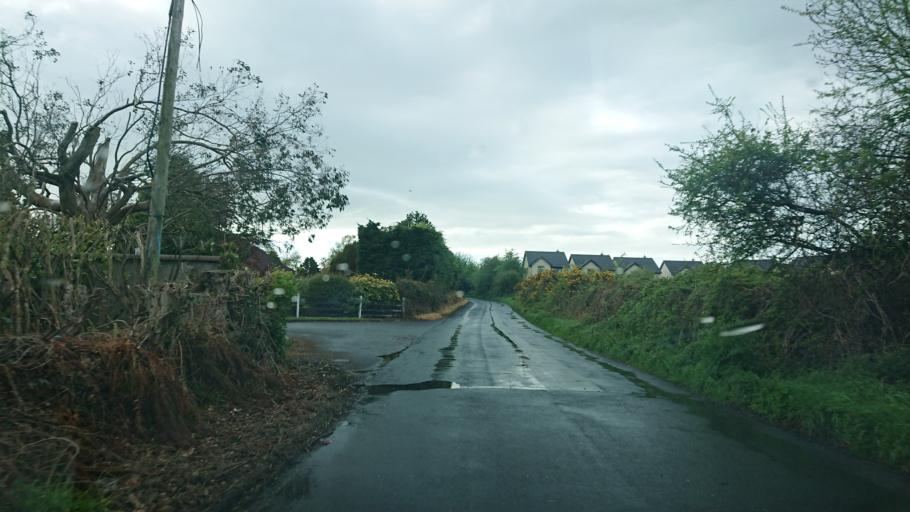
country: IE
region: Munster
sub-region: Waterford
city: Waterford
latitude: 52.2328
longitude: -7.0760
